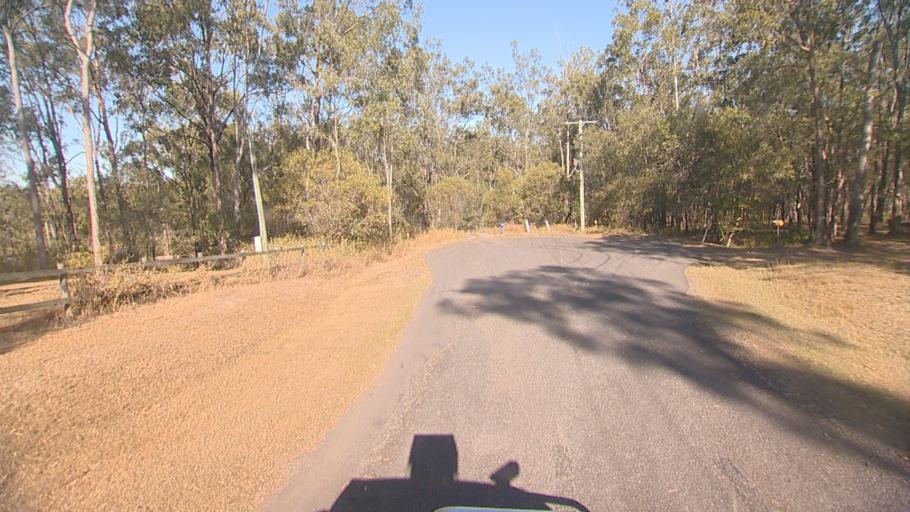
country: AU
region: Queensland
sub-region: Logan
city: Cedar Vale
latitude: -27.8472
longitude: 153.0574
